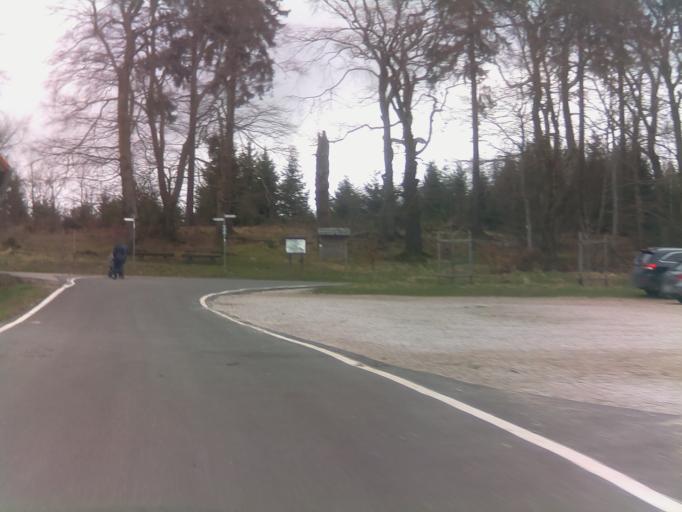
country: DE
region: Rheinland-Pfalz
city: Oberheimbach
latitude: 49.9952
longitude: 7.7701
